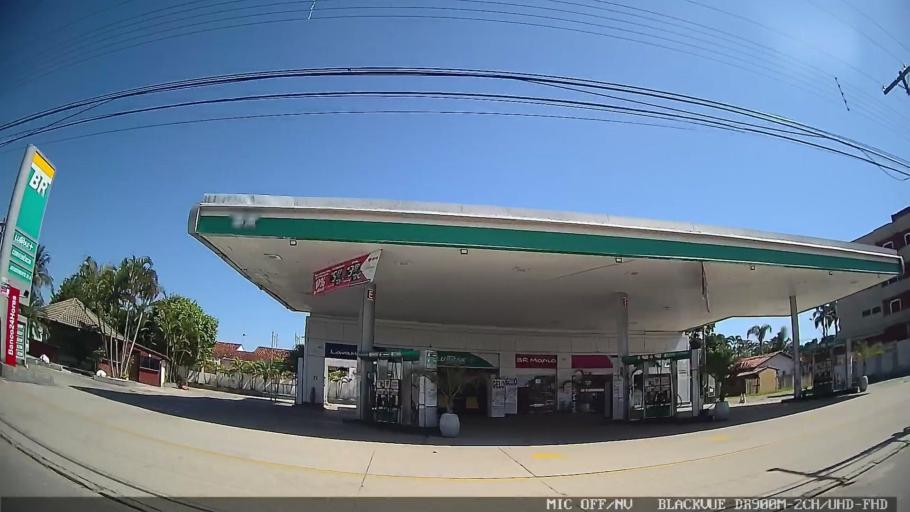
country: BR
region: Sao Paulo
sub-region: Peruibe
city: Peruibe
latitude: -24.2917
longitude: -46.9634
